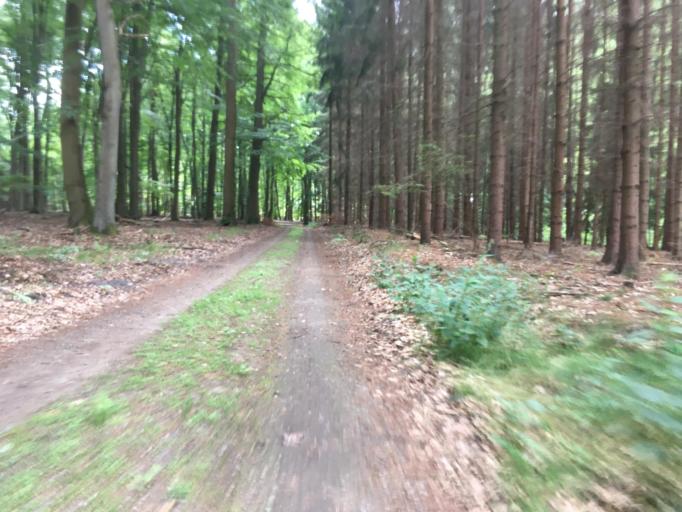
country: DE
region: Brandenburg
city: Althuttendorf
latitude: 52.9903
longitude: 13.8034
